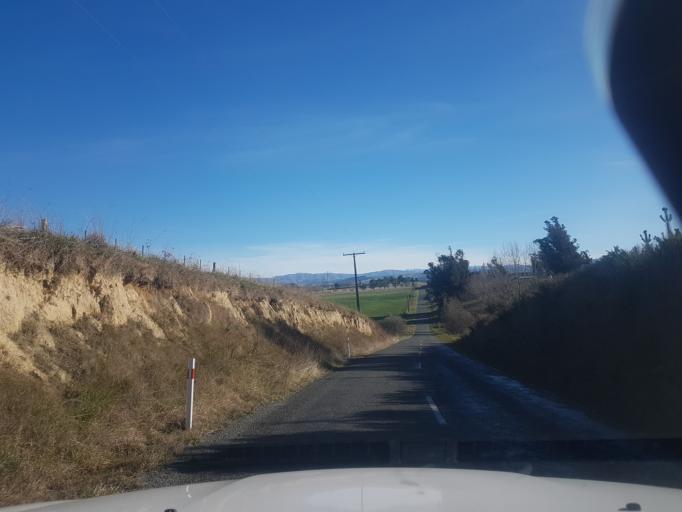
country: NZ
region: Canterbury
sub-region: Timaru District
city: Pleasant Point
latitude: -44.2512
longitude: 171.0613
